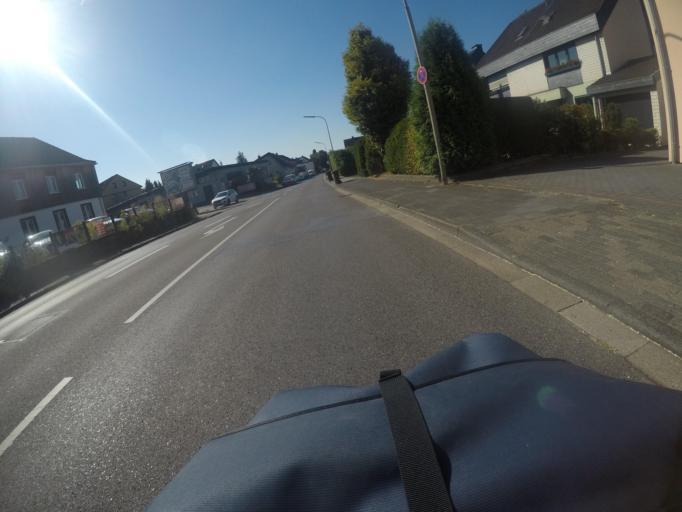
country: DE
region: North Rhine-Westphalia
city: Leichlingen
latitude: 51.1046
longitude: 6.9992
